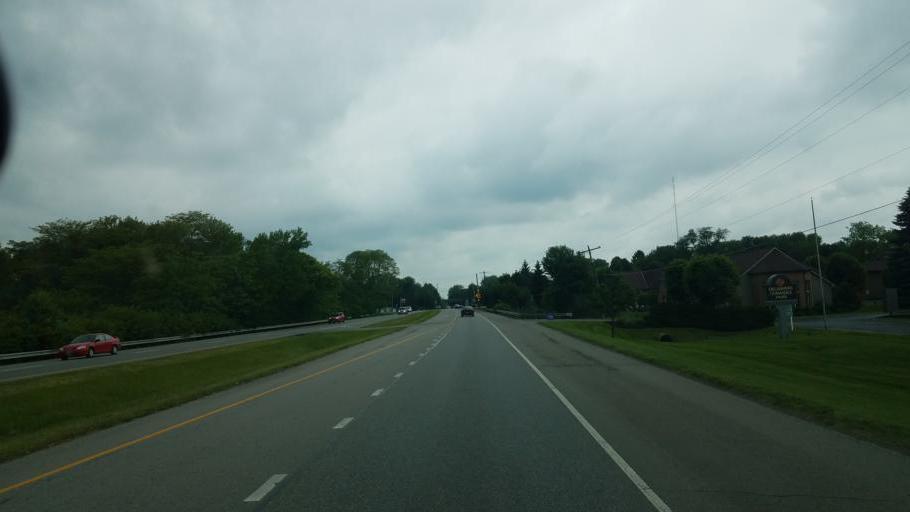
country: US
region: Ohio
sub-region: Delaware County
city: Delaware
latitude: 40.2962
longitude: -83.0410
